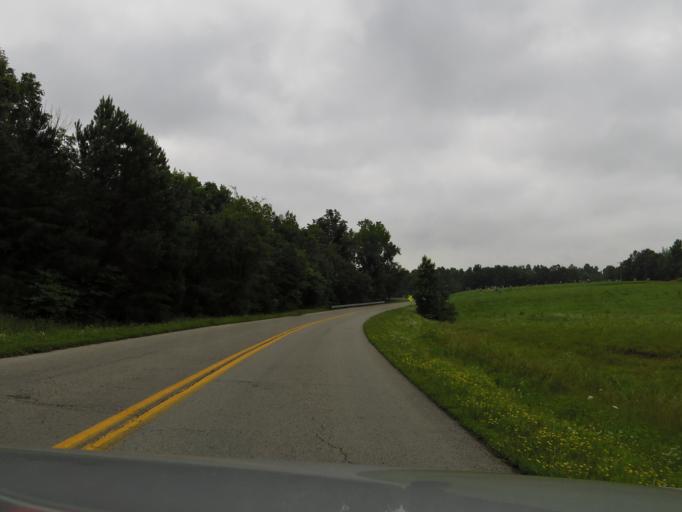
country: US
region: Kentucky
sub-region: Muhlenberg County
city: Morehead
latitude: 37.2693
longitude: -87.2850
